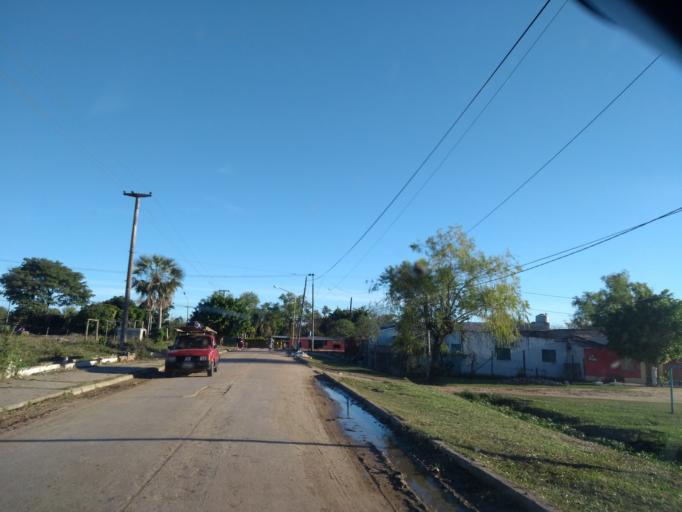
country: AR
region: Chaco
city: Puerto Vilelas
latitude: -27.5005
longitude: -58.9337
